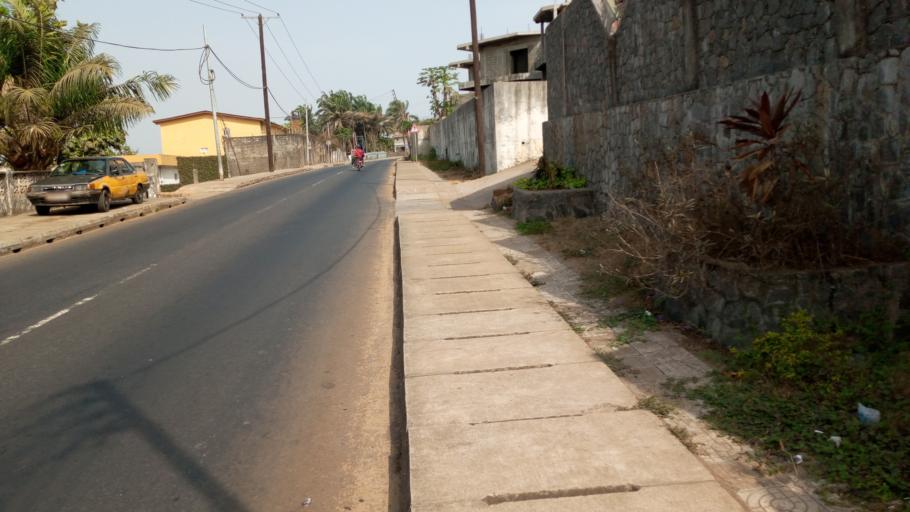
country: SL
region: Western Area
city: Freetown
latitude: 8.4796
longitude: -13.2631
